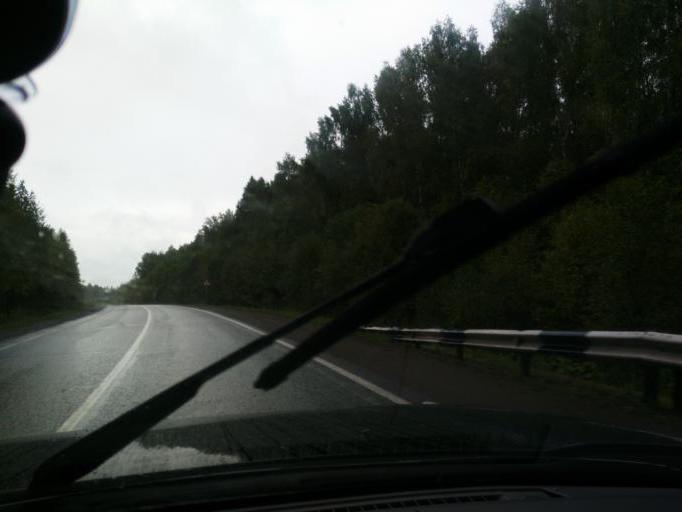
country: RU
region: Perm
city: Yugo-Kamskiy
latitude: 57.7433
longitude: 55.7127
